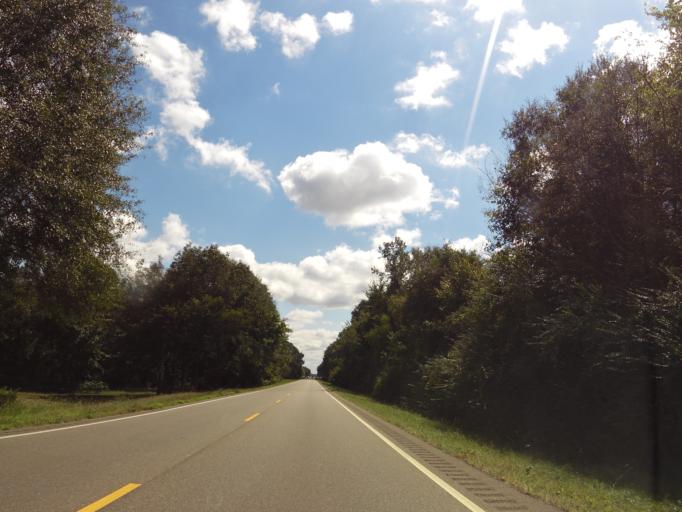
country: US
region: Alabama
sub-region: Dallas County
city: Selma
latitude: 32.4604
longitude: -87.0880
